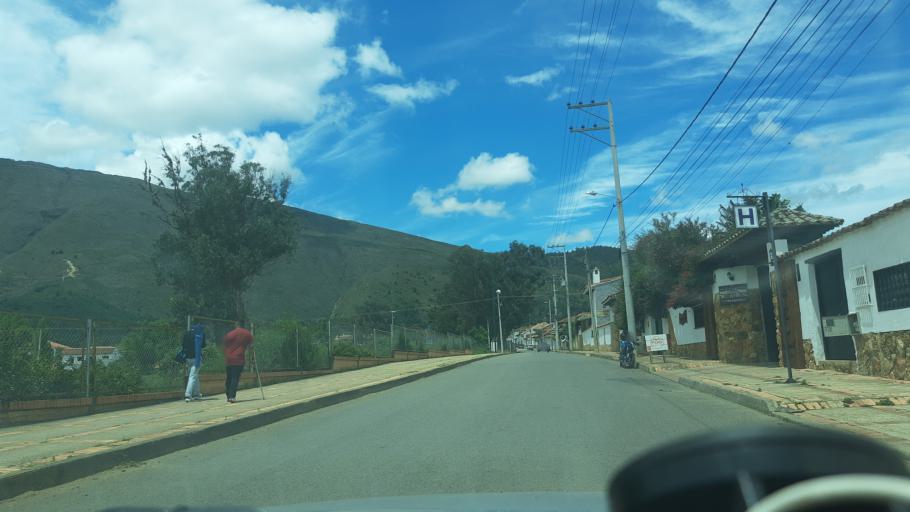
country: CO
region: Boyaca
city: Villa de Leiva
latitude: 5.6306
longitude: -73.5301
